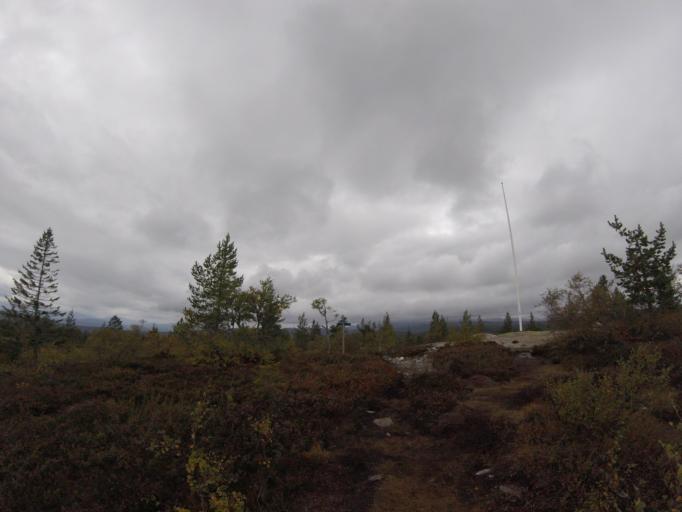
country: NO
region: Buskerud
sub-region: Flesberg
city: Lampeland
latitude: 59.7548
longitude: 9.4129
